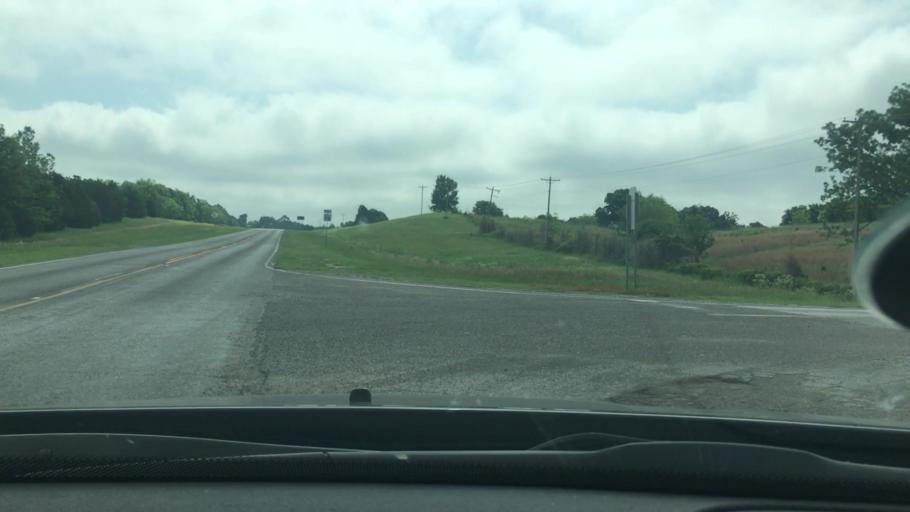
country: US
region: Oklahoma
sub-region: Johnston County
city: Tishomingo
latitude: 34.2303
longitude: -96.6350
